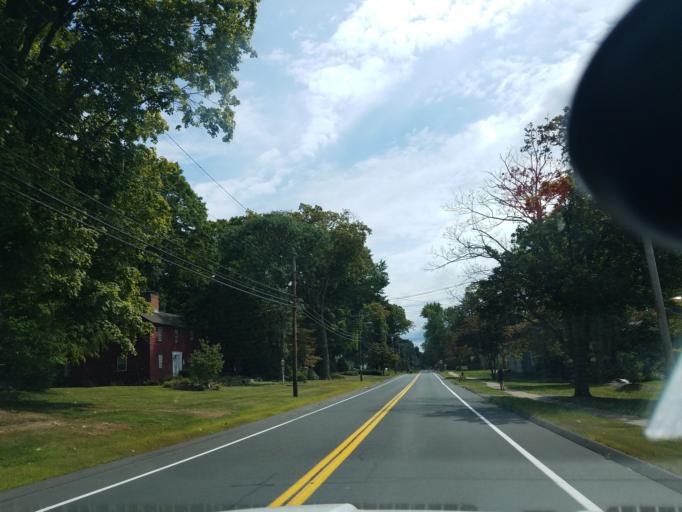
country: US
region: Connecticut
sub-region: Hartford County
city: Wethersfield
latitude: 41.6721
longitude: -72.6405
